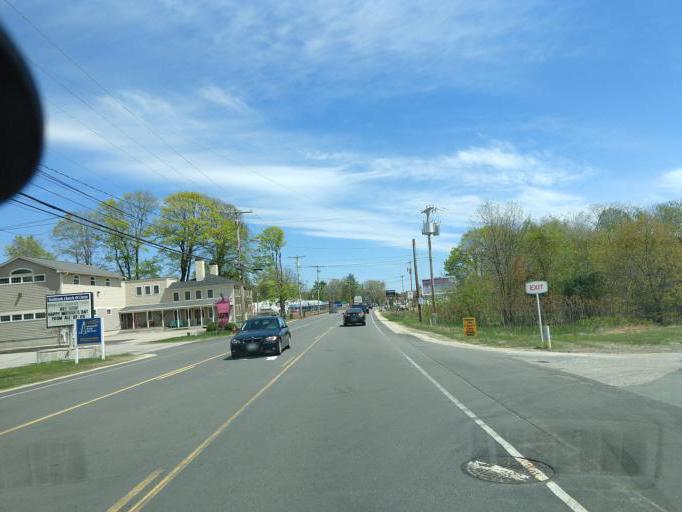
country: US
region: New Hampshire
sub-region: Rockingham County
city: Seabrook
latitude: 42.9010
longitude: -70.8699
